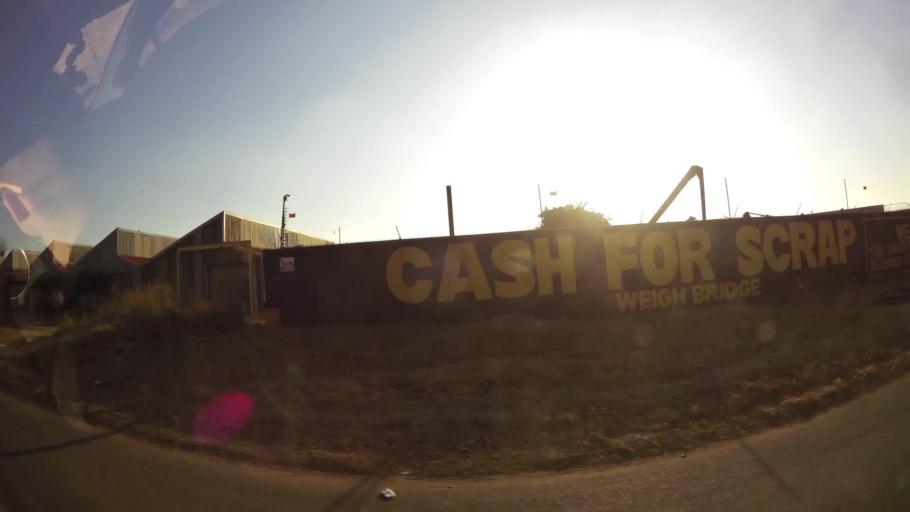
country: ZA
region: Gauteng
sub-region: West Rand District Municipality
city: Randfontein
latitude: -26.2021
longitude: 27.6957
